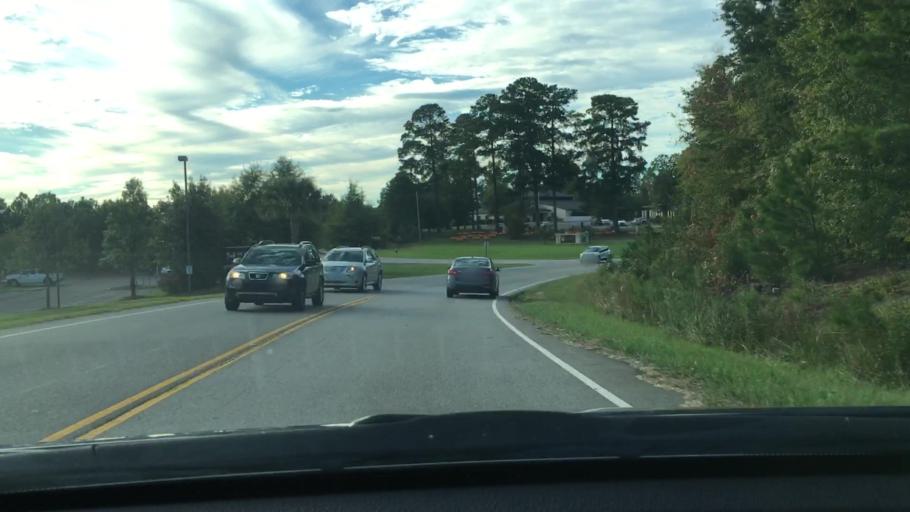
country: US
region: South Carolina
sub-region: Lexington County
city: Irmo
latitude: 34.0920
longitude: -81.1620
